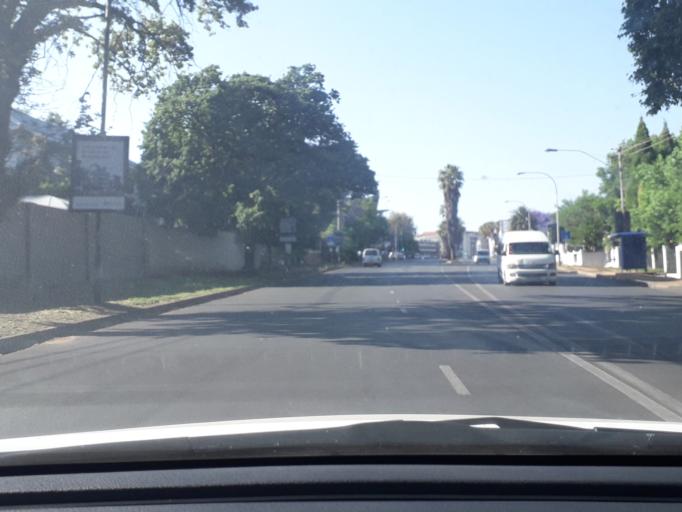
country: ZA
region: Gauteng
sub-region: City of Johannesburg Metropolitan Municipality
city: Johannesburg
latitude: -26.1415
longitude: 28.0356
